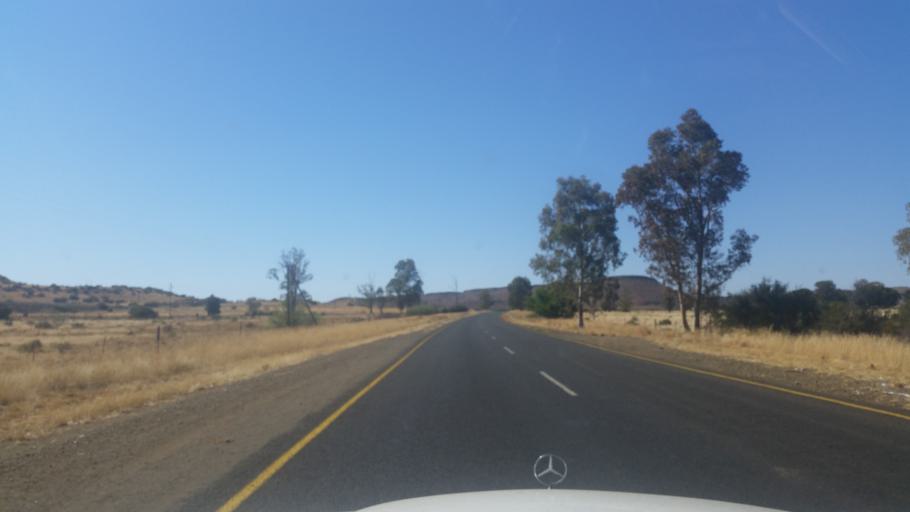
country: ZA
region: Orange Free State
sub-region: Xhariep District Municipality
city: Trompsburg
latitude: -30.4984
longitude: 26.0055
